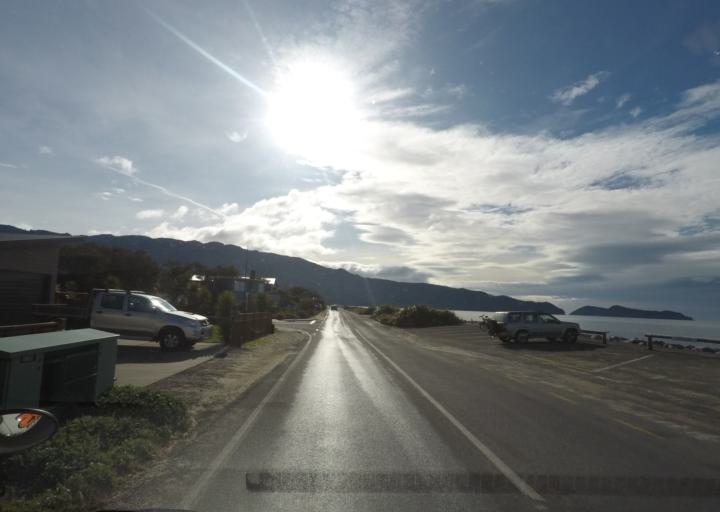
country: NZ
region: Tasman
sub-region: Tasman District
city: Motueka
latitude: -41.0078
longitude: 173.0089
